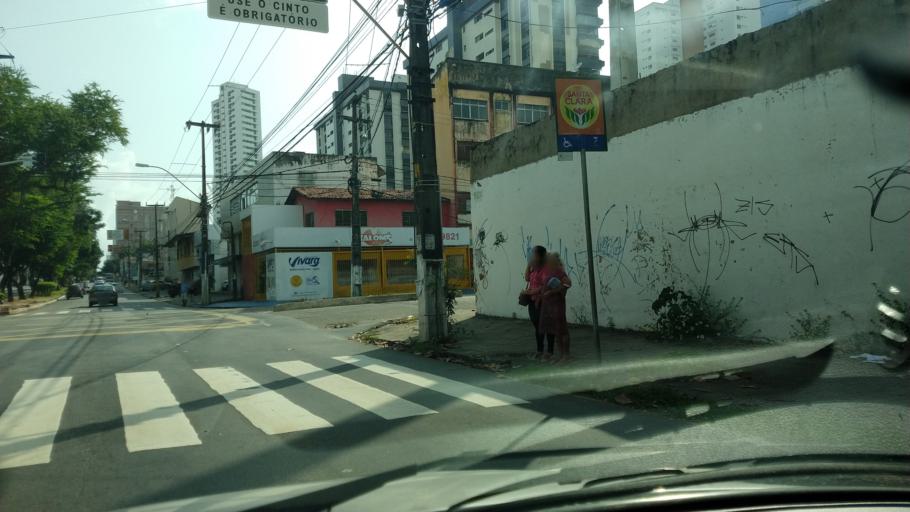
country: BR
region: Rio Grande do Norte
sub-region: Natal
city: Natal
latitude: -5.7941
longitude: -35.2036
